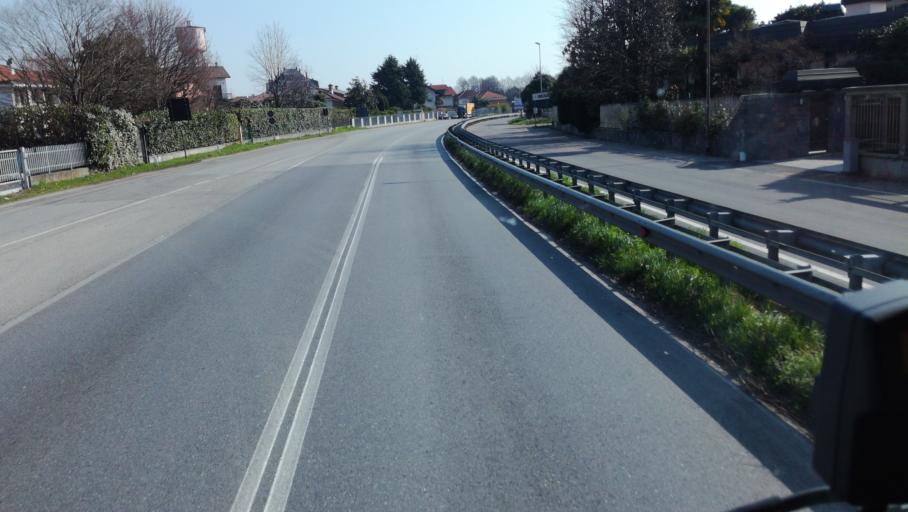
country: IT
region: Lombardy
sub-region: Citta metropolitana di Milano
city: Vanzago
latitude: 45.5310
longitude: 8.9886
